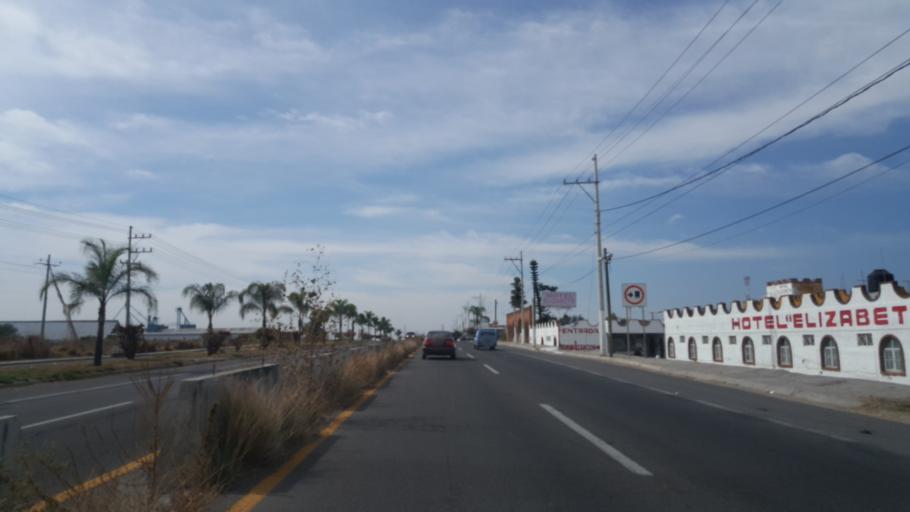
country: MX
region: Jalisco
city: San Juan de los Lagos
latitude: 21.2709
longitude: -102.3056
